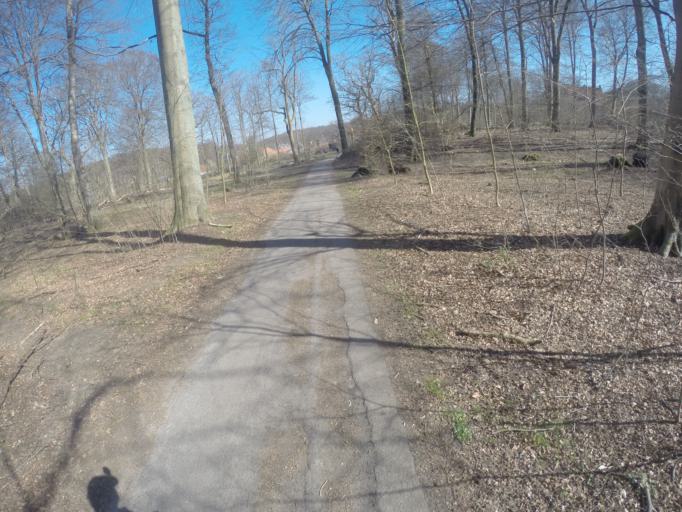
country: DK
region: Capital Region
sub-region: Rudersdal Kommune
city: Trorod
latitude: 55.8042
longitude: 12.5563
